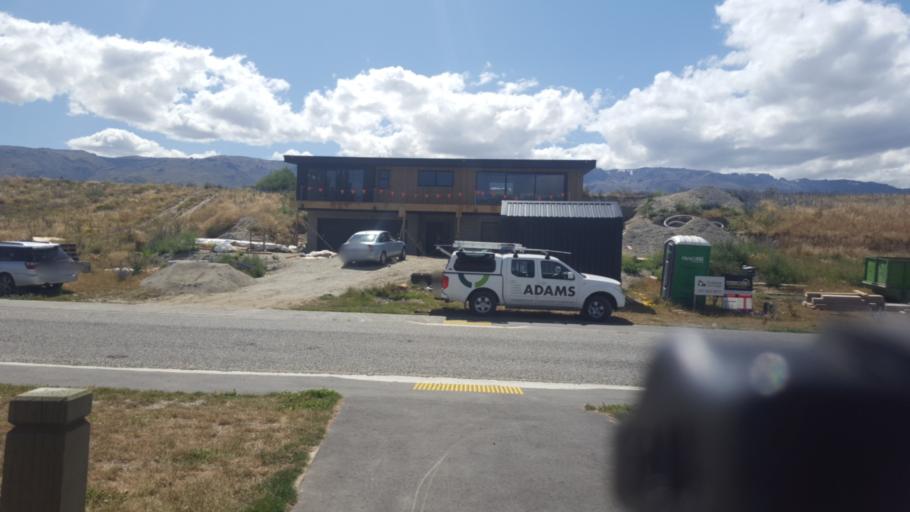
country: NZ
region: Otago
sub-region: Queenstown-Lakes District
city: Wanaka
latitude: -44.9748
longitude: 169.2407
